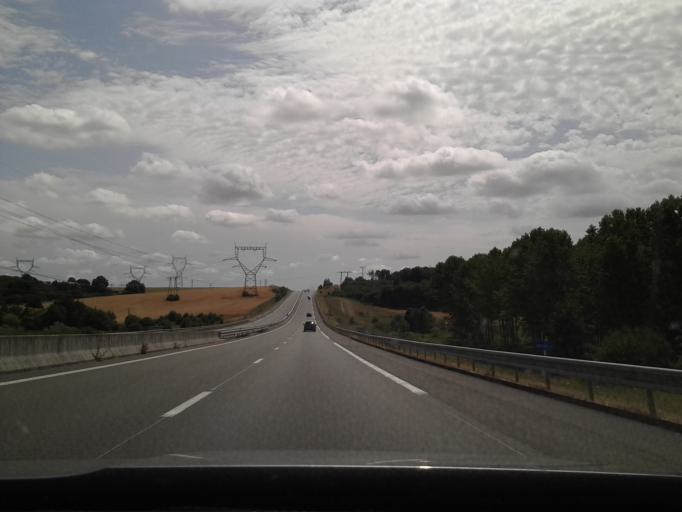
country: FR
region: Centre
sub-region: Departement d'Indre-et-Loire
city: Cerelles
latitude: 47.4873
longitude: 0.6726
